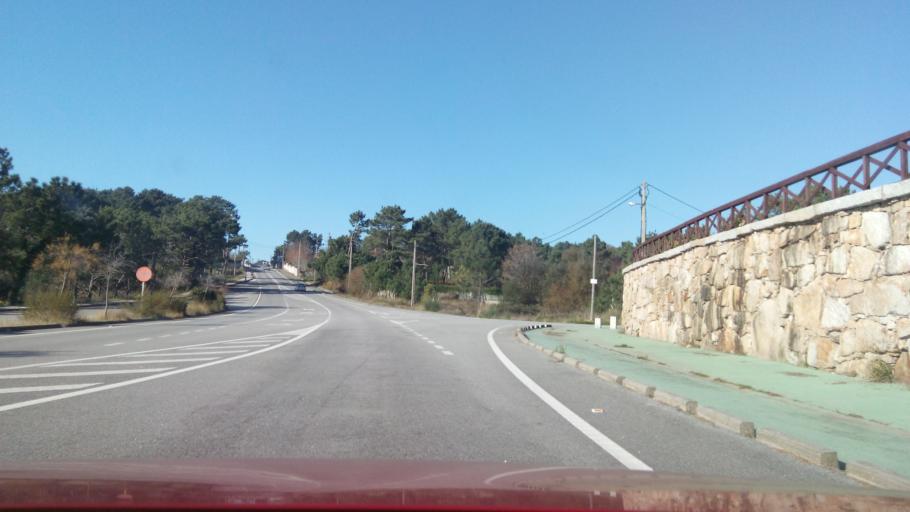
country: ES
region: Galicia
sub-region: Provincia de Pontevedra
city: O Grove
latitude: 42.4627
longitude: -8.8989
